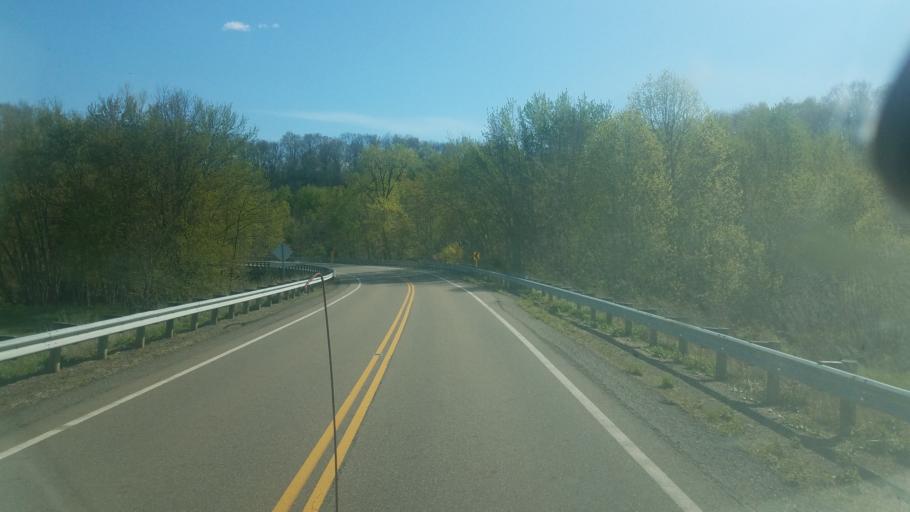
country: US
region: Ohio
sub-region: Coshocton County
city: Coshocton
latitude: 40.3666
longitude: -81.9863
